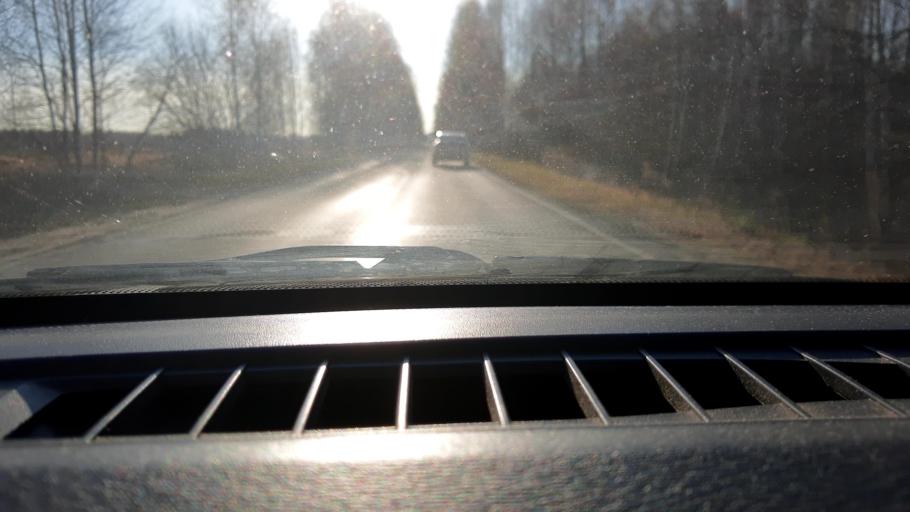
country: RU
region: Nizjnij Novgorod
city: Neklyudovo
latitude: 56.4831
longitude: 43.8683
